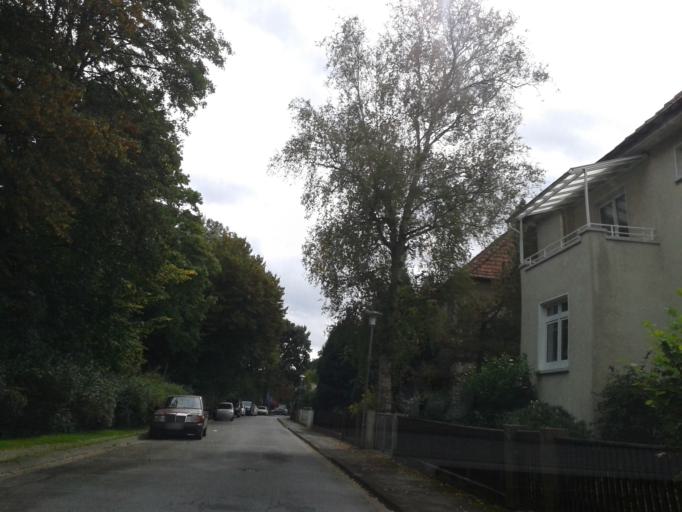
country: DE
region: Lower Saxony
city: Bad Pyrmont
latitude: 51.9841
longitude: 9.2454
